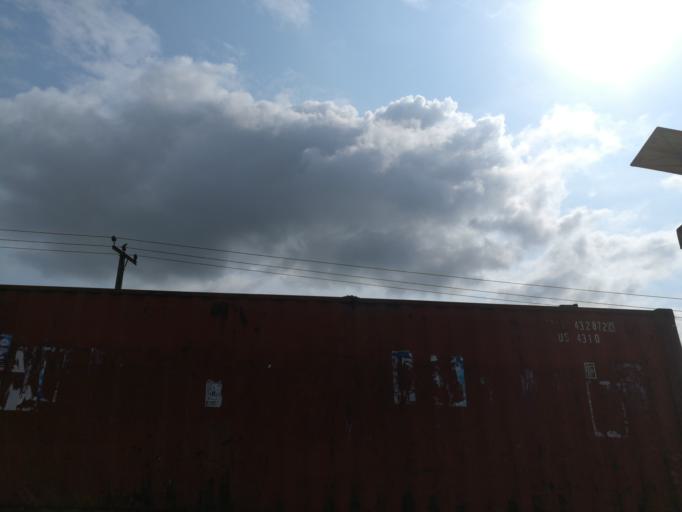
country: NG
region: Rivers
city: Okrika
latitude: 4.7566
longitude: 7.0850
